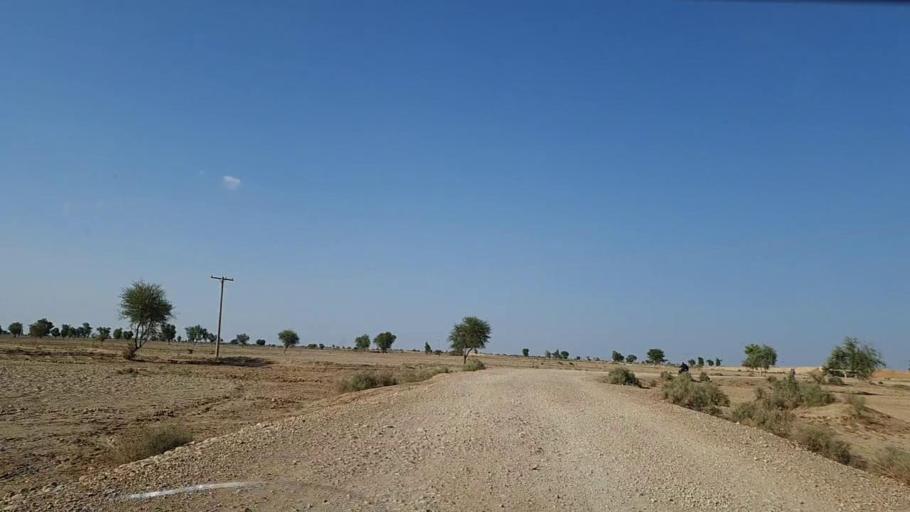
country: PK
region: Sindh
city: Johi
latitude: 26.5304
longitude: 67.5301
